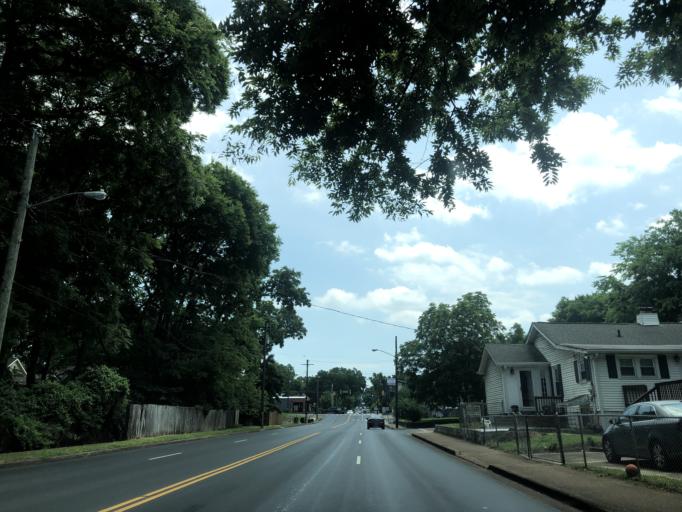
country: US
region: Tennessee
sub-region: Davidson County
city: Nashville
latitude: 36.1845
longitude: -86.7564
